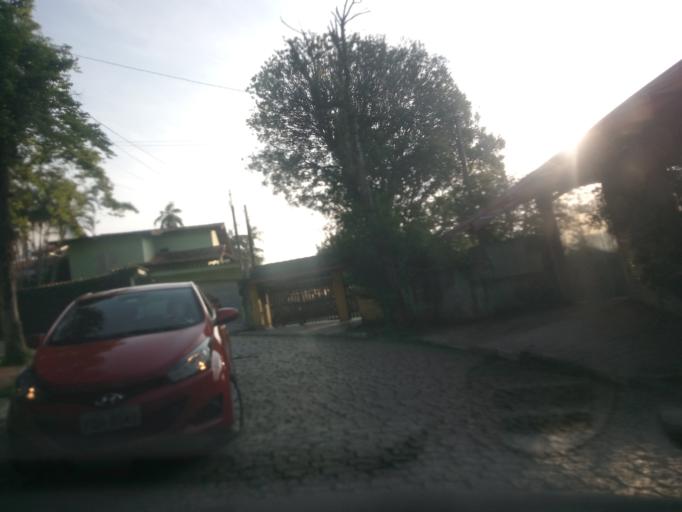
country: BR
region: Sao Paulo
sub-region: Sao Bernardo Do Campo
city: Sao Bernardo do Campo
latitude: -23.7793
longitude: -46.5328
